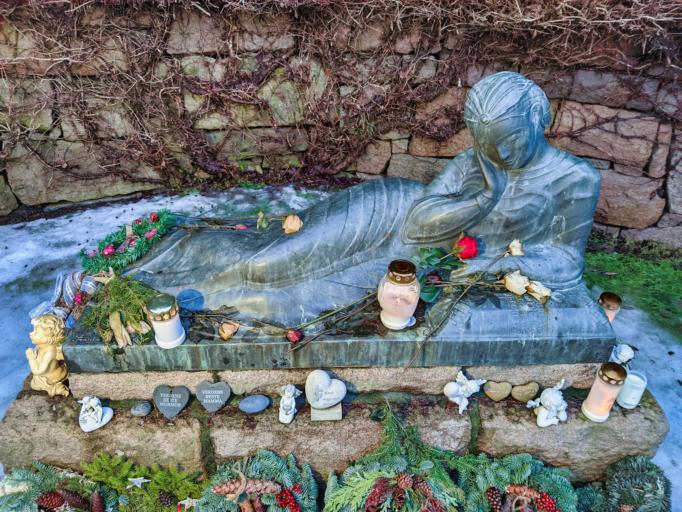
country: NO
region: Oslo
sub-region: Oslo
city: Oslo
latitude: 59.9219
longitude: 10.8178
